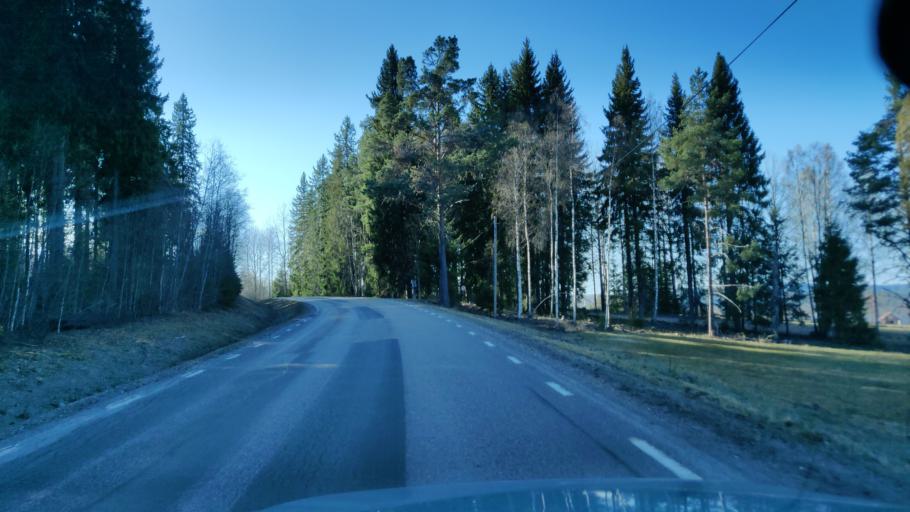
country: SE
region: Vaermland
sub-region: Munkfors Kommun
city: Munkfors
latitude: 59.9691
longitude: 13.4631
